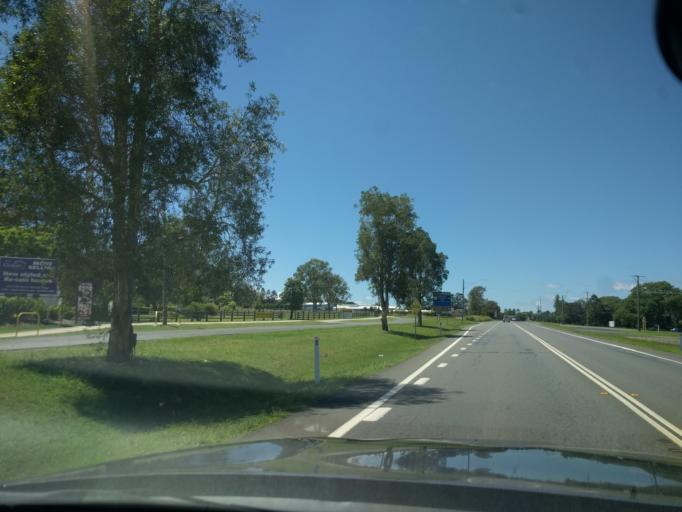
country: AU
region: Queensland
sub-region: Logan
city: Cedar Vale
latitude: -27.9668
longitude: 152.9962
